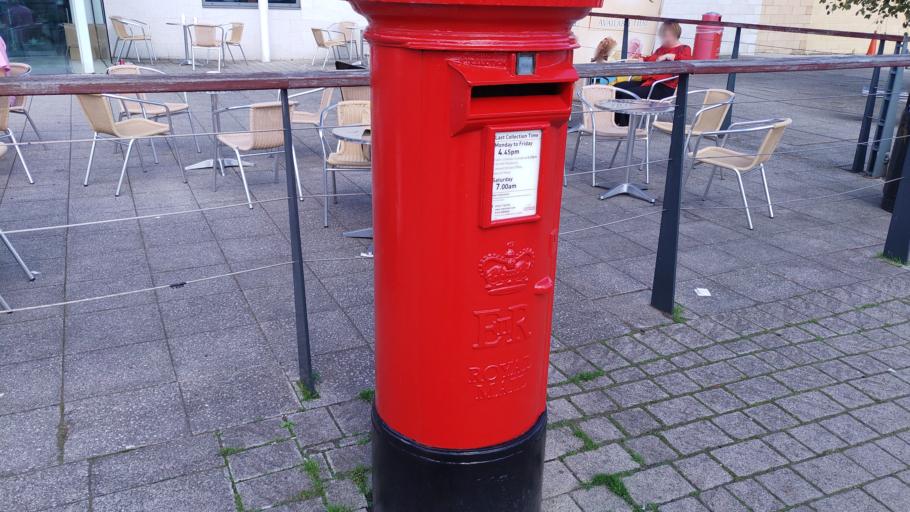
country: GB
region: England
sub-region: Staffordshire
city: Norton Canes
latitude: 52.6648
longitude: -1.9674
